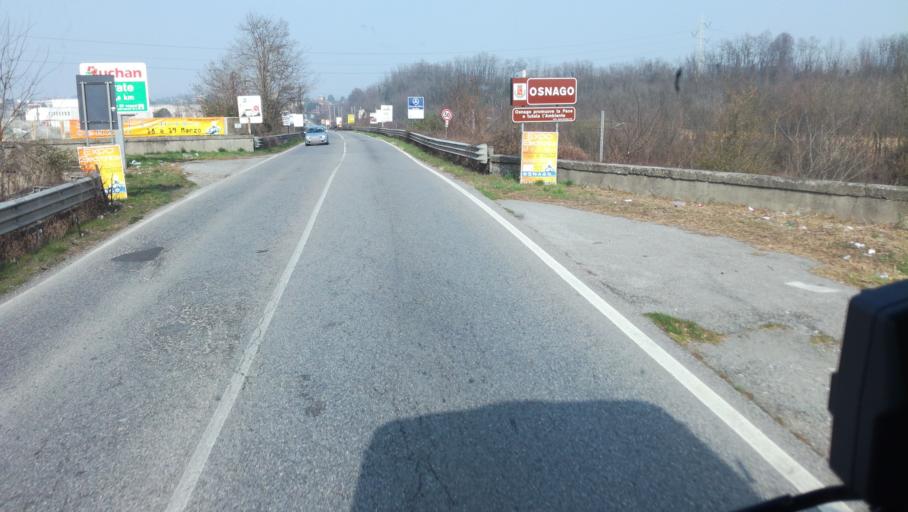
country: IT
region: Lombardy
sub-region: Provincia di Lecco
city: Lomagna
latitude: 45.6618
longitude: 9.3831
